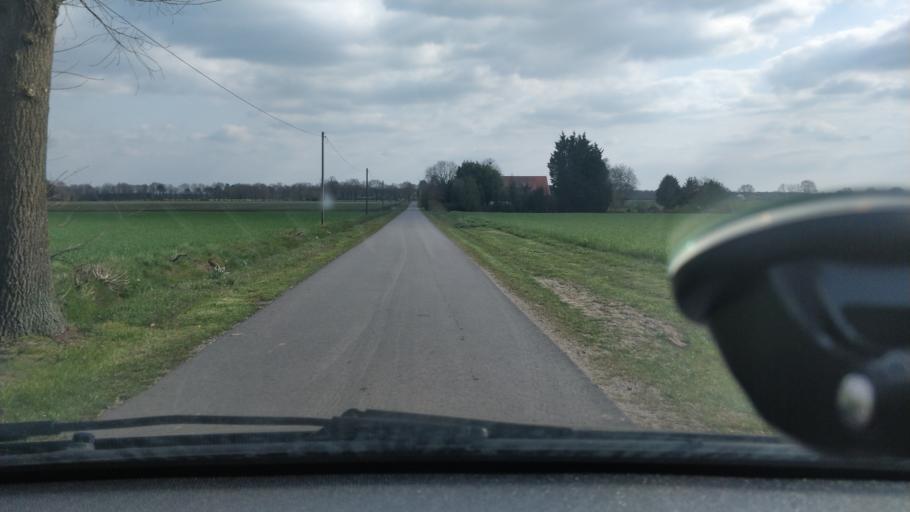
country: NL
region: Gelderland
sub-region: Gemeente Aalten
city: Bredevoort
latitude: 51.8943
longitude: 6.6294
